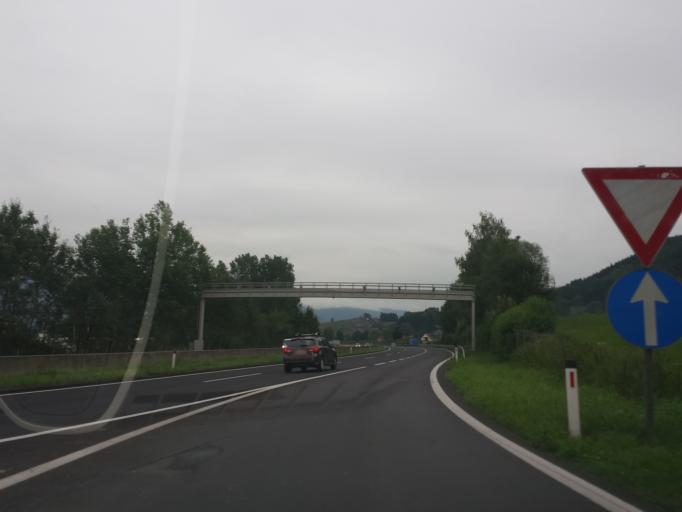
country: AT
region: Styria
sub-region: Politischer Bezirk Bruck-Muerzzuschlag
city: Frauenberg
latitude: 47.4514
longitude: 15.3409
